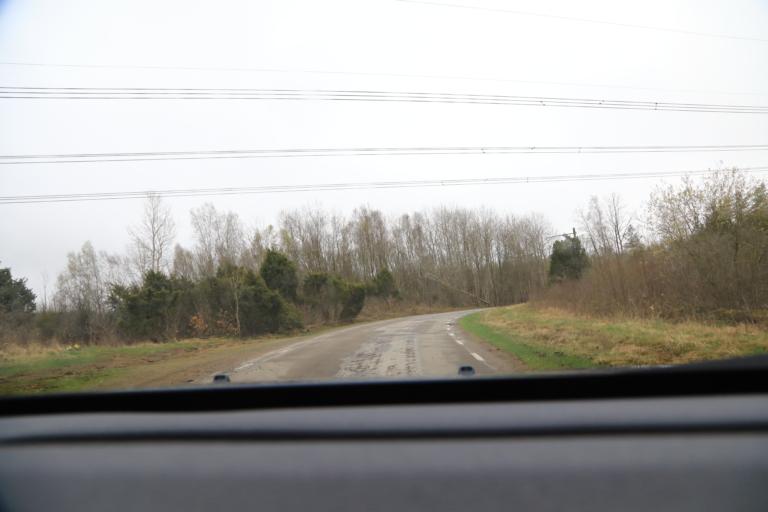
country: SE
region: Halland
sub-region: Kungsbacka Kommun
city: Frillesas
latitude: 57.2830
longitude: 12.2056
